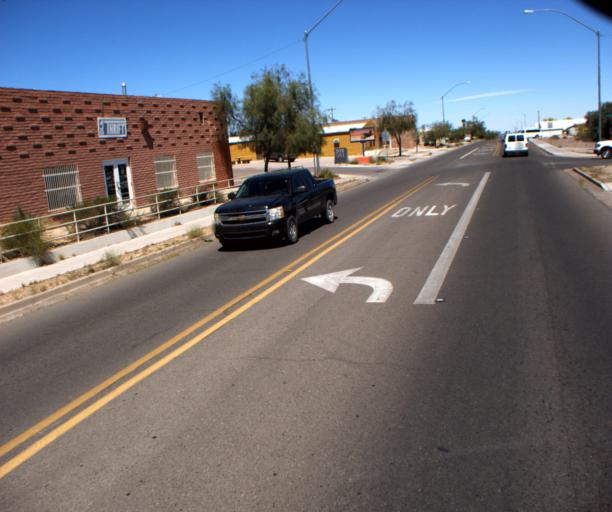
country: US
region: Arizona
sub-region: Pima County
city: Ajo
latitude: 32.3784
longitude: -112.8724
